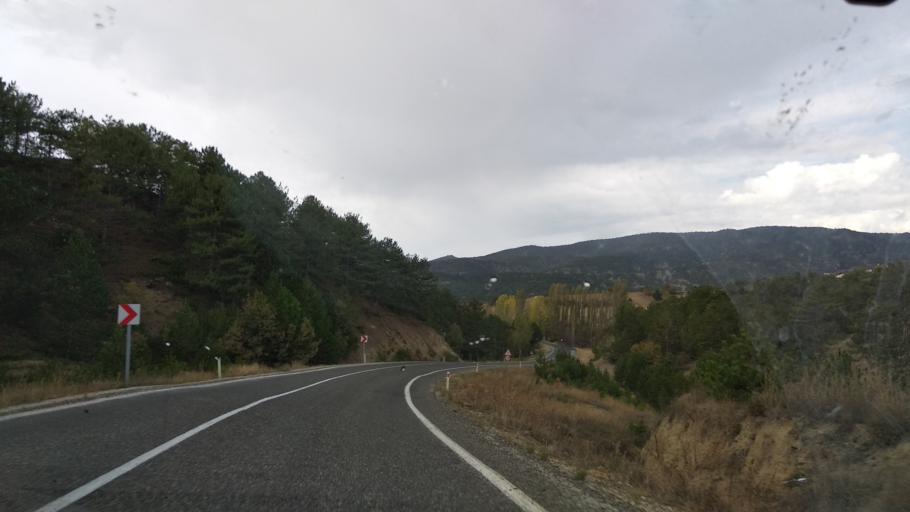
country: TR
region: Bolu
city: Seben
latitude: 40.3373
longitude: 31.4297
